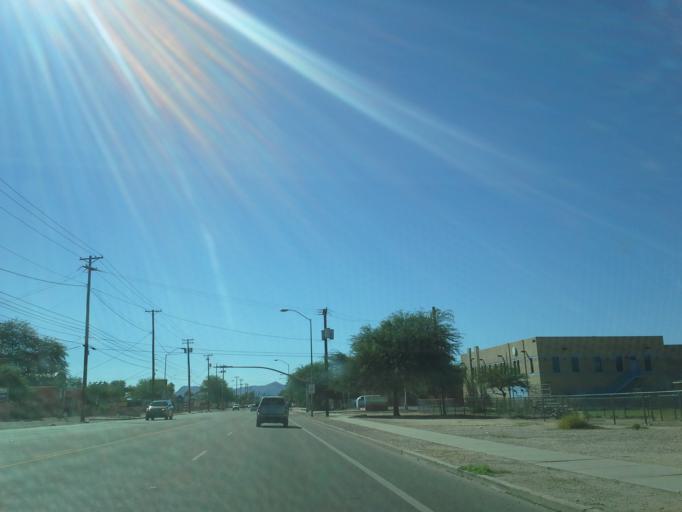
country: US
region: Arizona
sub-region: Pima County
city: Tucson
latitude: 32.2505
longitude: -110.9234
